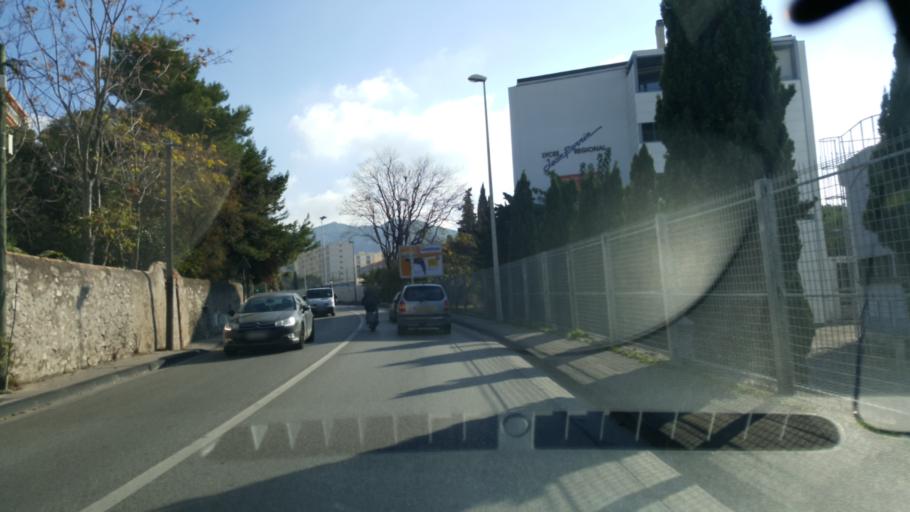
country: FR
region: Provence-Alpes-Cote d'Azur
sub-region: Departement des Bouches-du-Rhone
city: Marseille 10
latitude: 43.2744
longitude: 5.4267
